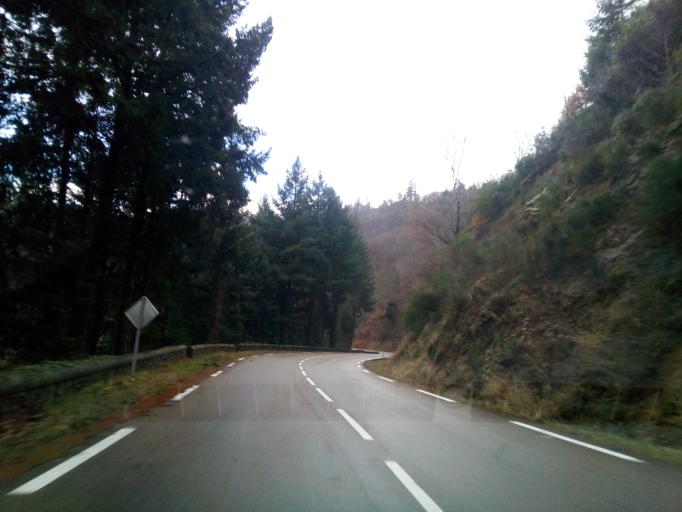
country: FR
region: Rhone-Alpes
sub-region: Departement de l'Ardeche
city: Le Cheylard
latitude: 44.8809
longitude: 4.5101
